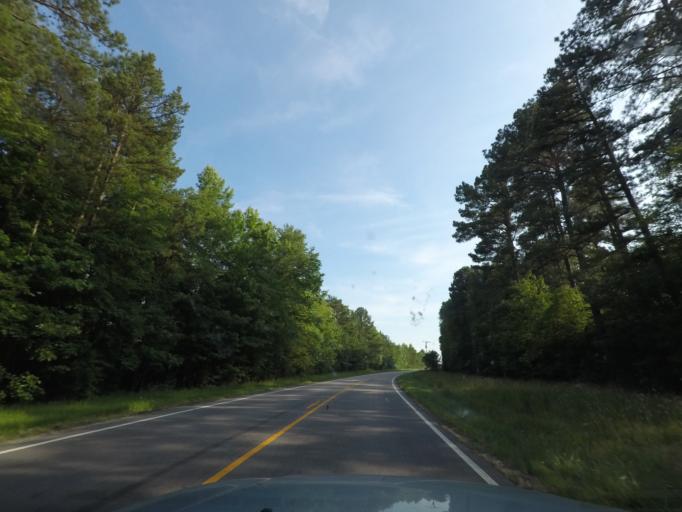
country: US
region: North Carolina
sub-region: Granville County
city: Oxford
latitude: 36.4235
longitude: -78.5842
